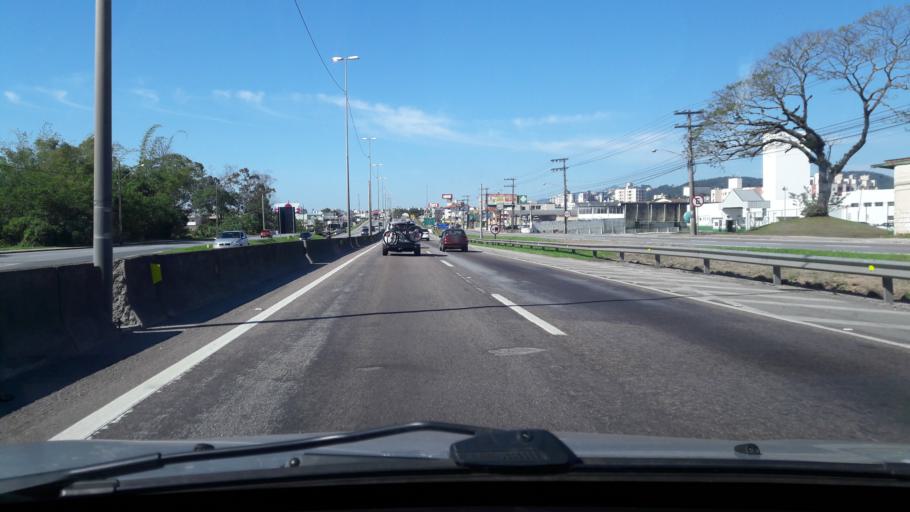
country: BR
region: Santa Catarina
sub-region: Sao Jose
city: Campinas
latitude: -27.5489
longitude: -48.6197
